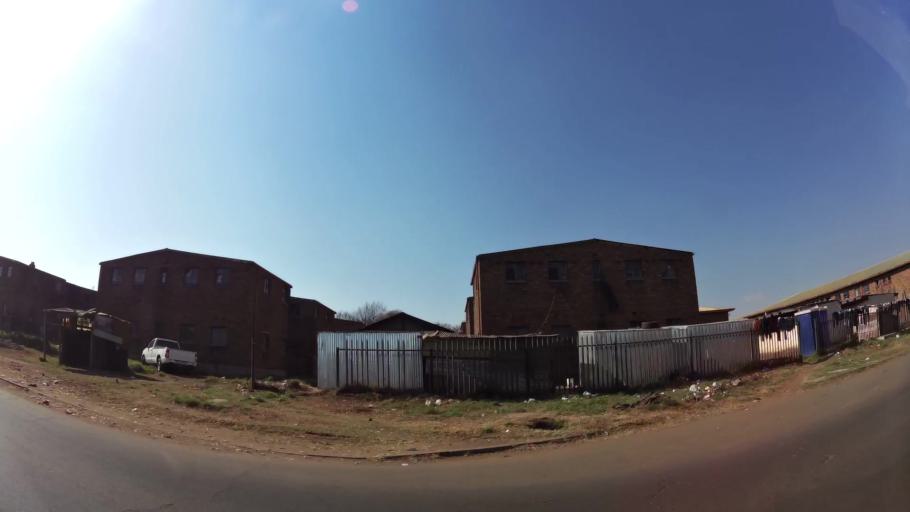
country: ZA
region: Gauteng
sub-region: Ekurhuleni Metropolitan Municipality
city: Benoni
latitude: -26.2119
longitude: 28.2957
